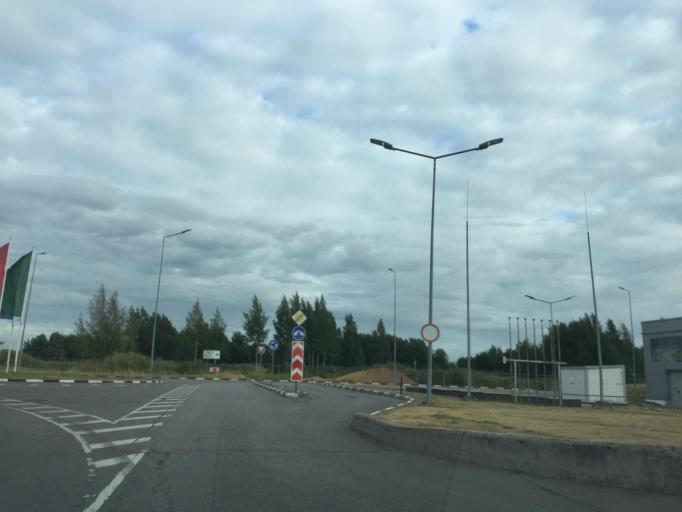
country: RU
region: Leningrad
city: Bugry
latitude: 60.0907
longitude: 30.3855
